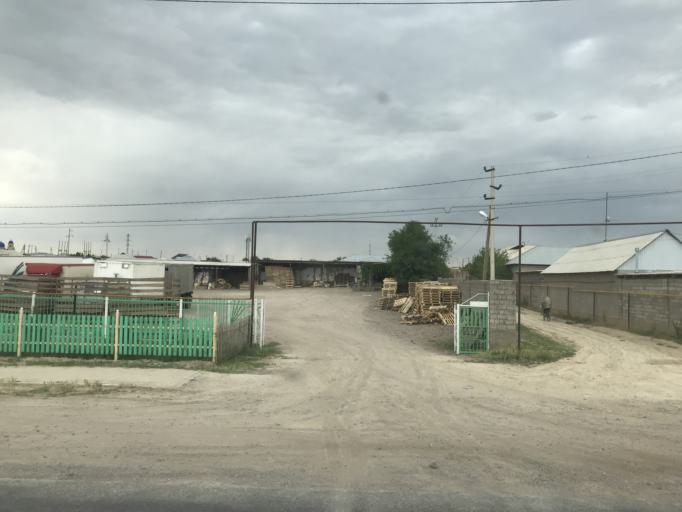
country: KZ
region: Ongtustik Qazaqstan
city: Saryaghash
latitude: 41.4304
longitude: 69.1058
